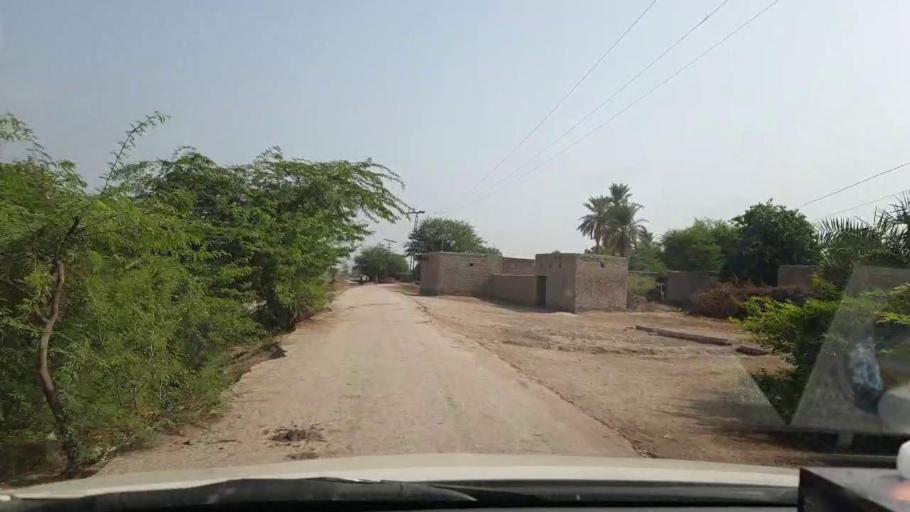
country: PK
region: Sindh
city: Shikarpur
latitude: 27.9819
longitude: 68.6659
